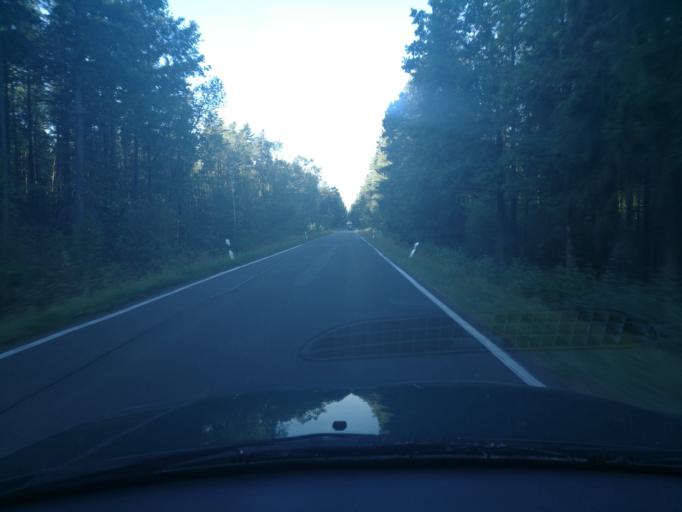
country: DE
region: Bavaria
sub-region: Regierungsbezirk Mittelfranken
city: Hessdorf
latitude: 49.6157
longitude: 10.9383
